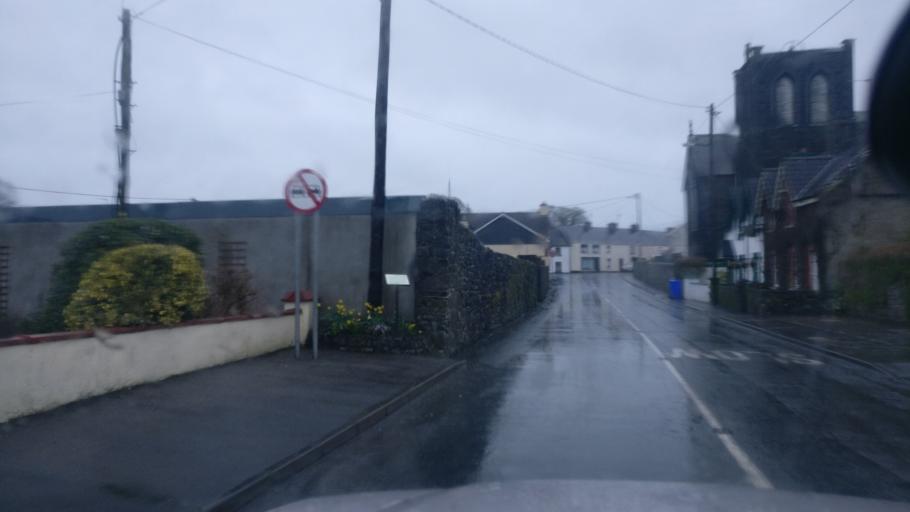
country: IE
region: Connaught
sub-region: County Galway
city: Ballinasloe
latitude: 53.3044
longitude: -8.3181
